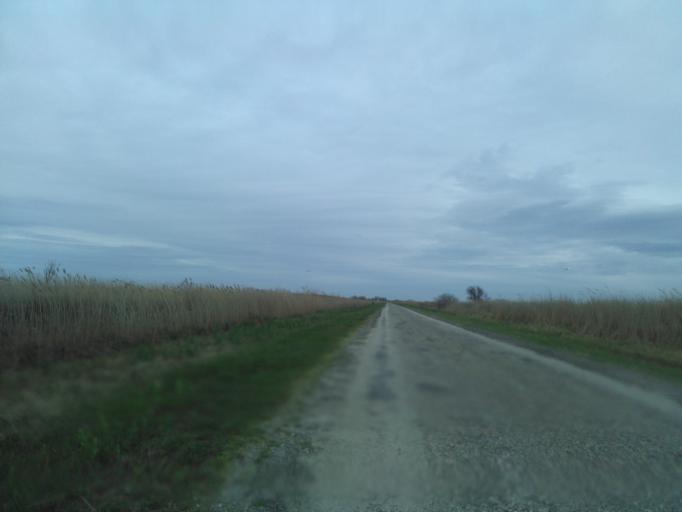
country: FR
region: Provence-Alpes-Cote d'Azur
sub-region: Departement des Bouches-du-Rhone
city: Arles
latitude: 43.5921
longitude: 4.5430
